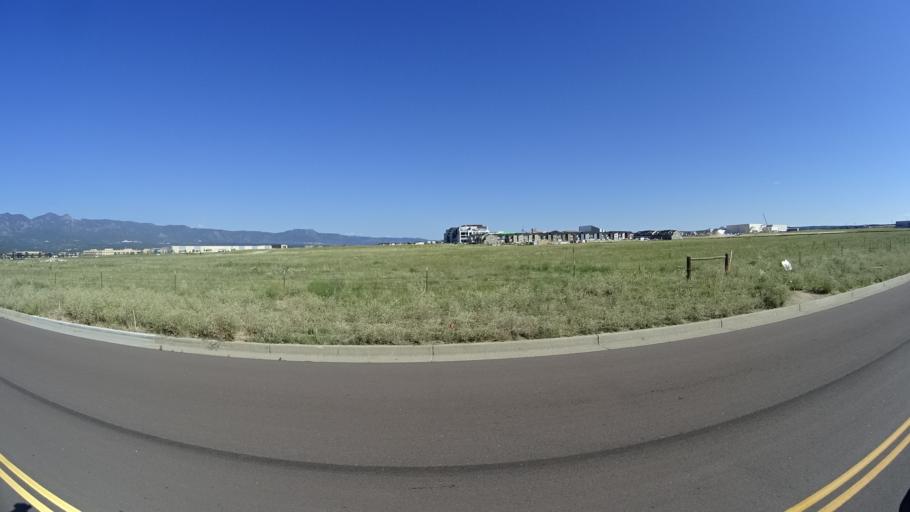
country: US
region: Colorado
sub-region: El Paso County
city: Gleneagle
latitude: 38.9823
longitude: -104.7920
